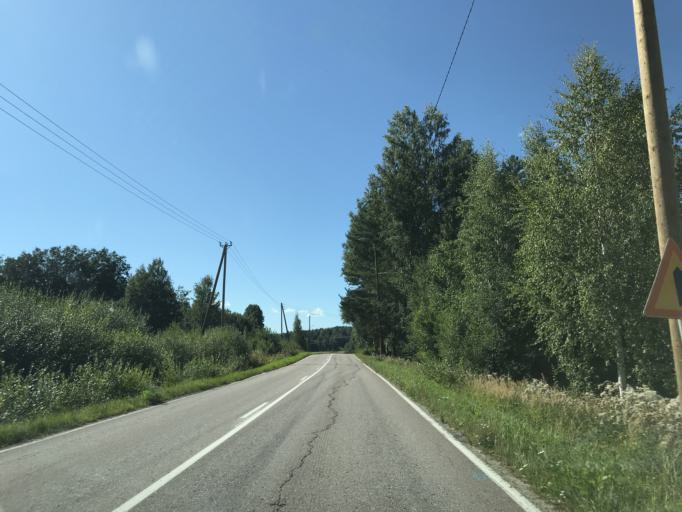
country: FI
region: Uusimaa
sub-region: Helsinki
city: Nurmijaervi
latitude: 60.4907
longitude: 24.6273
